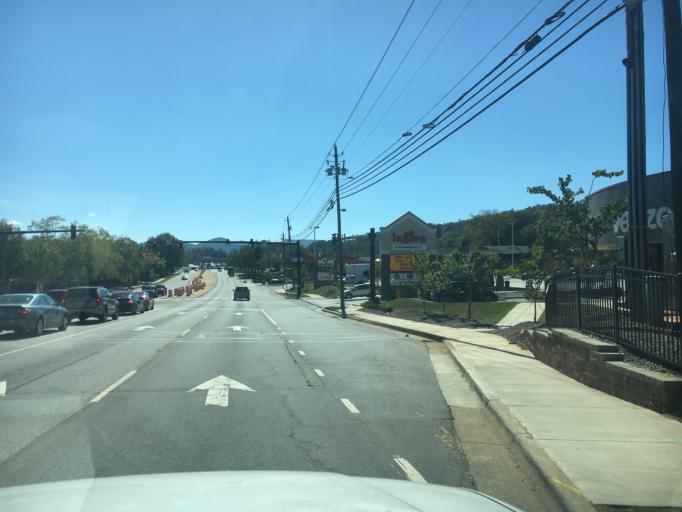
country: US
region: North Carolina
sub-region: Buncombe County
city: Bent Creek
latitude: 35.5312
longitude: -82.6056
